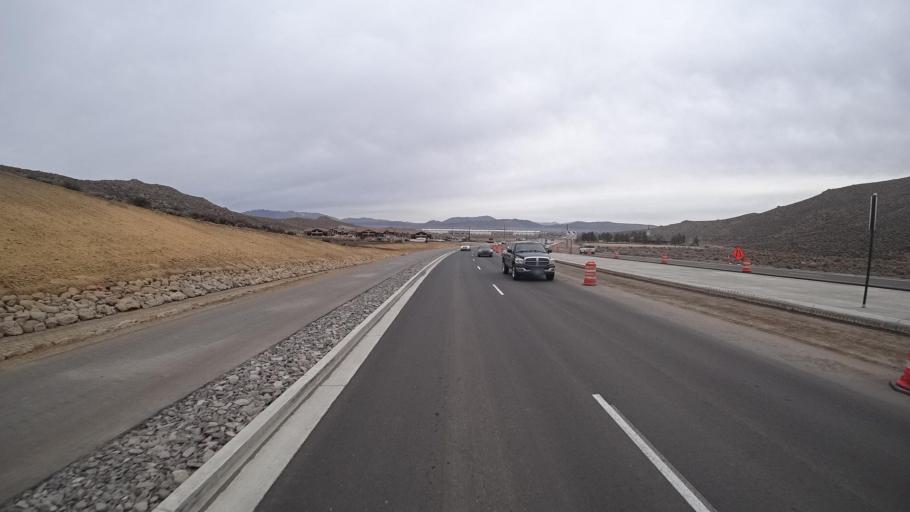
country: US
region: Nevada
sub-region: Washoe County
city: Lemmon Valley
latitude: 39.6198
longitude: -119.8488
